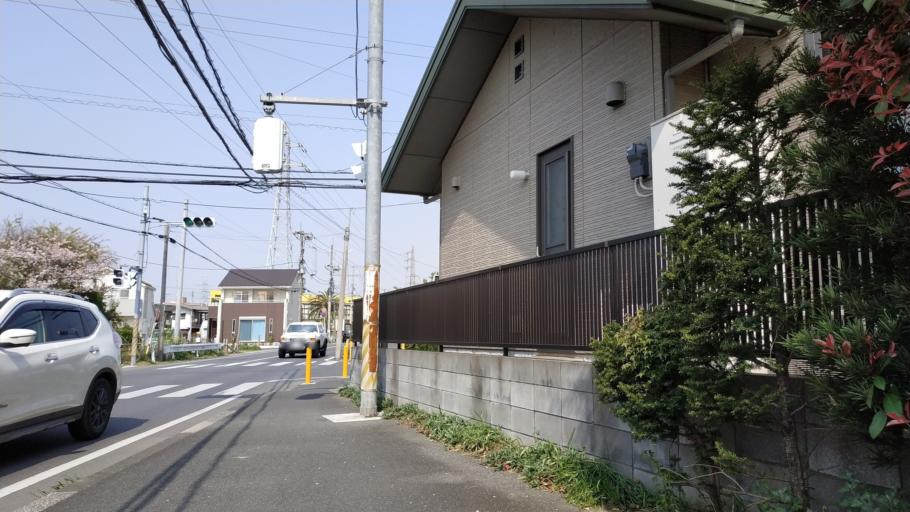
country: JP
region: Chiba
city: Ichihara
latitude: 35.5070
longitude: 140.0905
